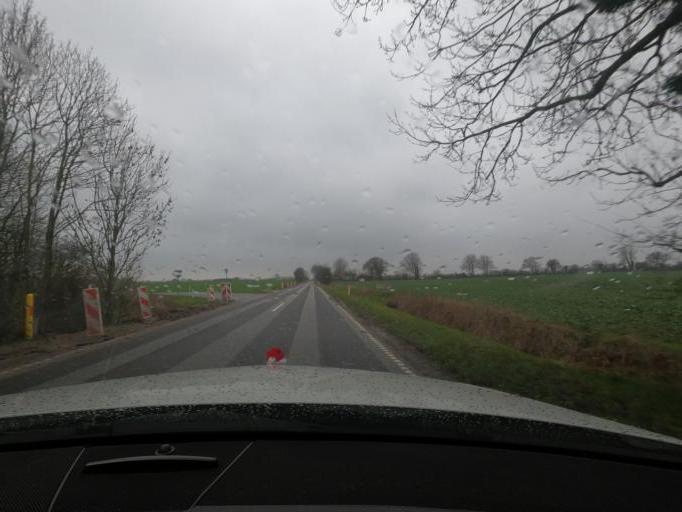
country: DK
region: South Denmark
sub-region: Haderslev Kommune
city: Starup
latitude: 55.2291
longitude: 9.6353
